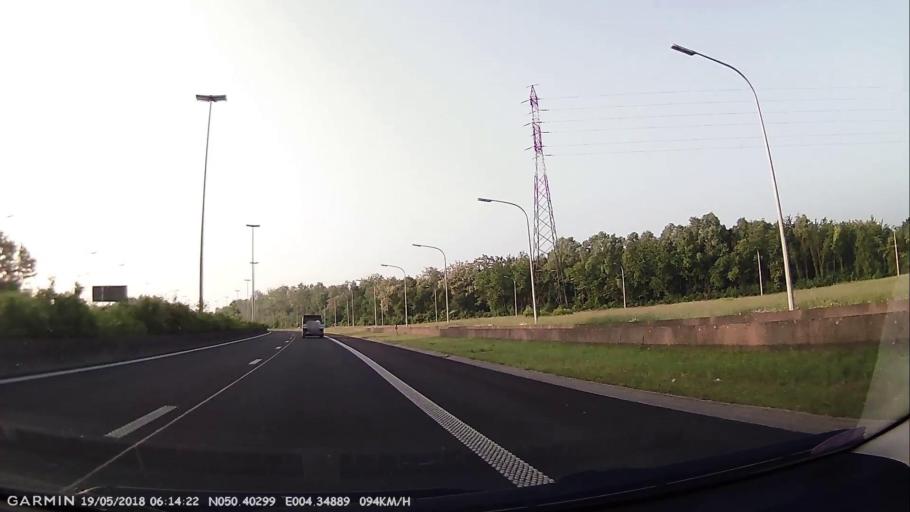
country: BE
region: Wallonia
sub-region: Province du Hainaut
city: Courcelles
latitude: 50.4028
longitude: 4.3491
